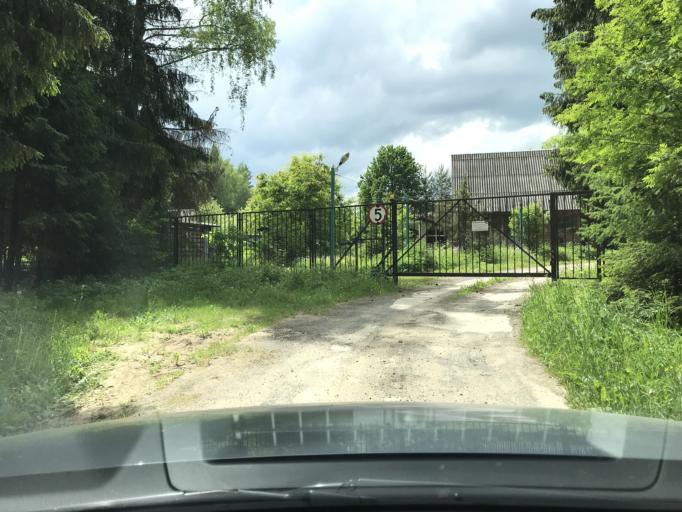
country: RU
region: Moskovskaya
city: Vereya
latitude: 55.3175
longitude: 36.3231
